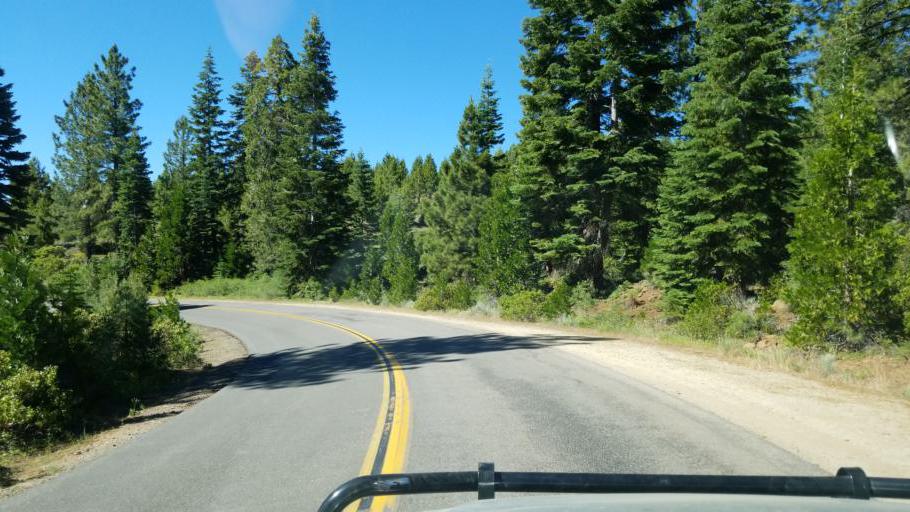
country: US
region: California
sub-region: Lassen County
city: Susanville
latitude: 40.4906
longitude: -120.7455
